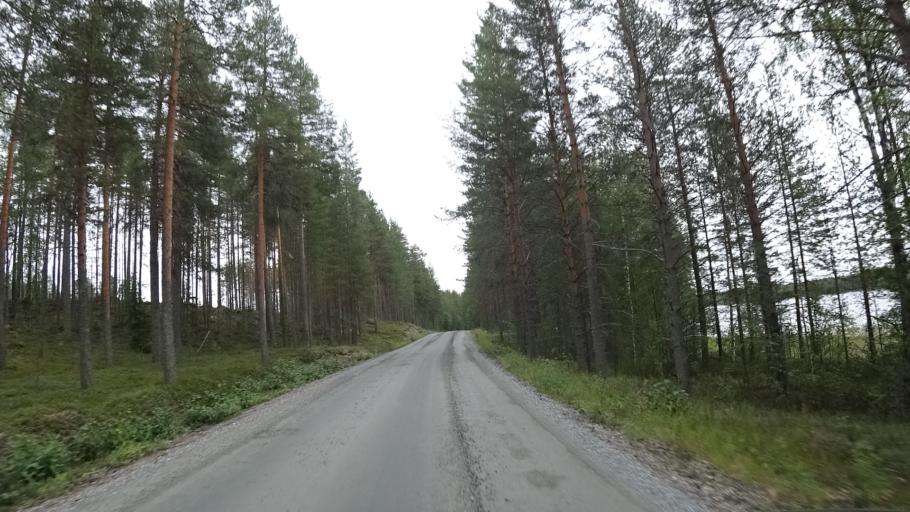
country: FI
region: North Karelia
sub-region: Pielisen Karjala
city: Lieksa
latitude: 63.3842
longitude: 30.3397
